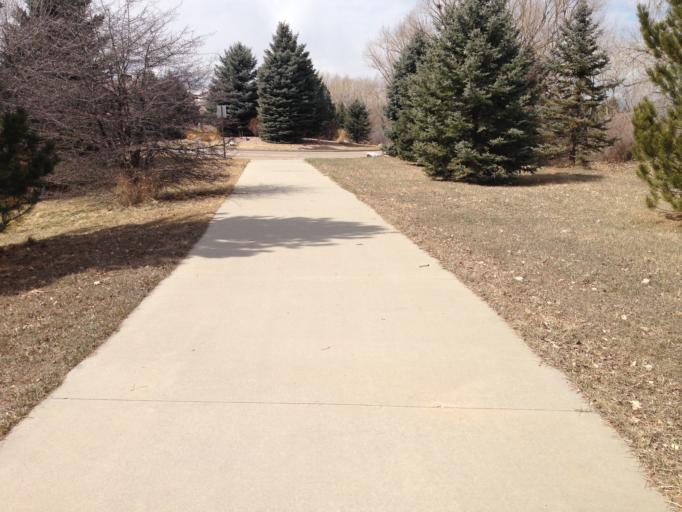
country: US
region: Colorado
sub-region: Boulder County
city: Louisville
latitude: 40.0086
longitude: -105.1417
